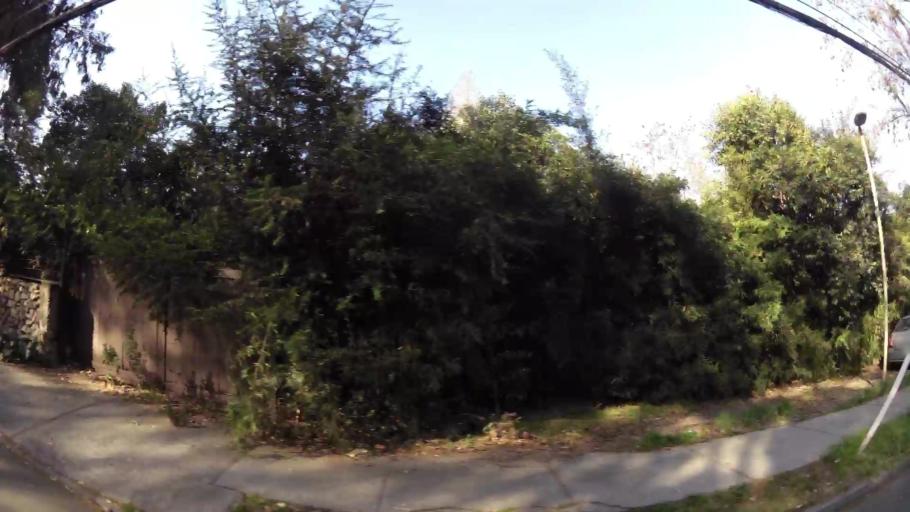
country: CL
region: Santiago Metropolitan
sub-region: Provincia de Santiago
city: Villa Presidente Frei, Nunoa, Santiago, Chile
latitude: -33.3749
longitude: -70.5089
